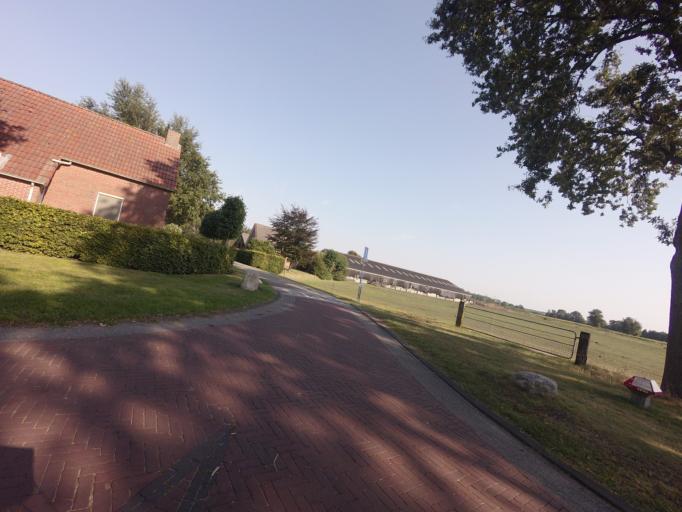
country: NL
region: Groningen
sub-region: Gemeente Zuidhorn
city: Aduard
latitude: 53.1690
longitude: 6.4777
